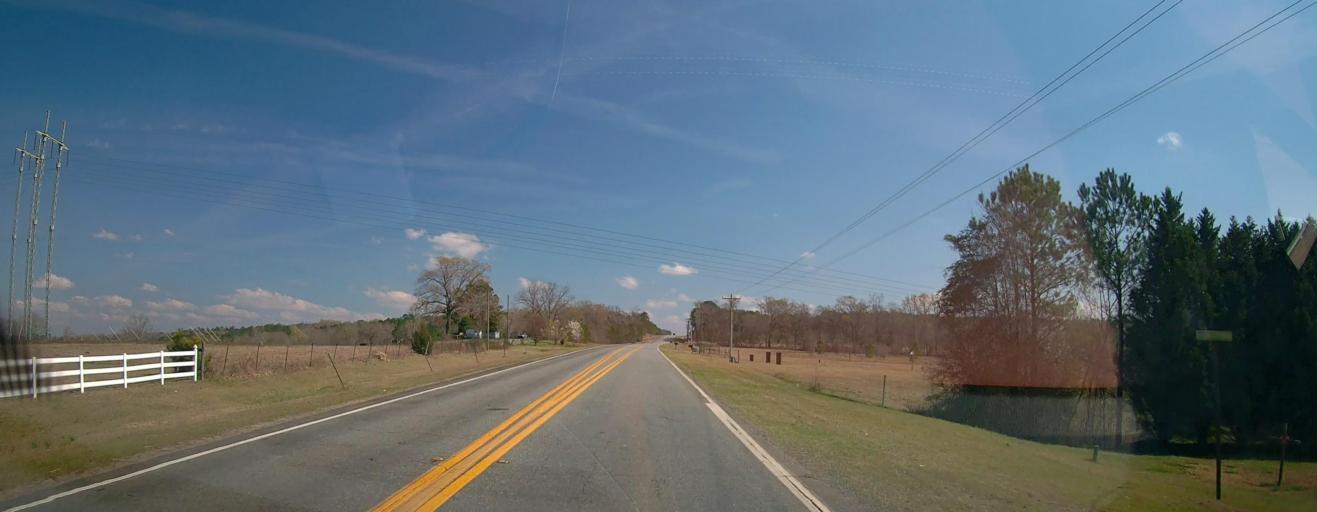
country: US
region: Georgia
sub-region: Wilkinson County
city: Gordon
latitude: 32.9229
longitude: -83.3963
